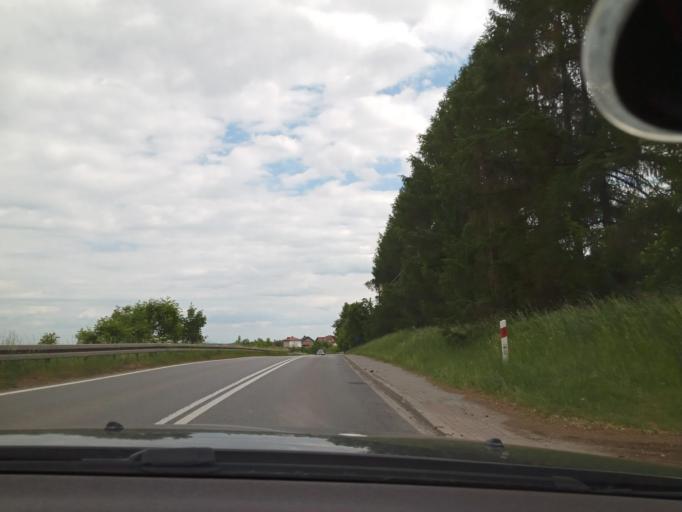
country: PL
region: Lesser Poland Voivodeship
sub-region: Powiat wielicki
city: Trabki
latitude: 49.9541
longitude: 20.1571
